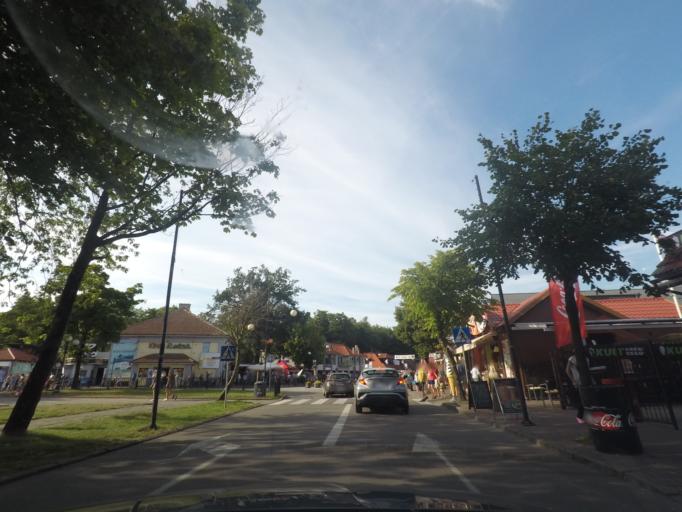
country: PL
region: Pomeranian Voivodeship
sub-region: Powiat leborski
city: Leba
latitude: 54.7613
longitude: 17.5552
